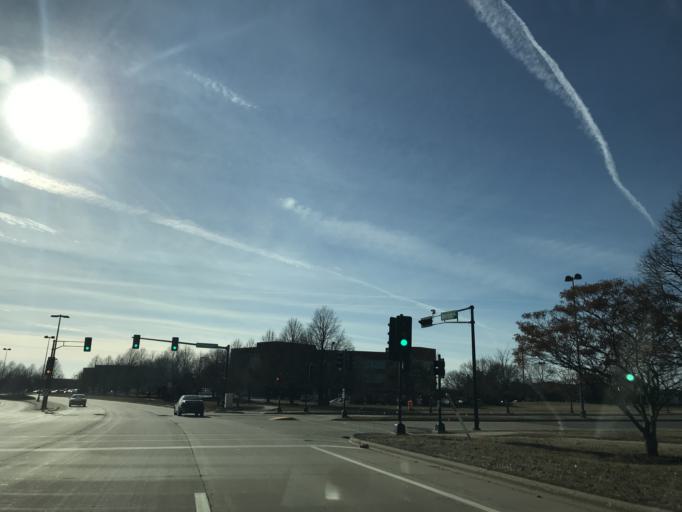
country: US
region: Wisconsin
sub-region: Dane County
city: Sun Prairie
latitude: 43.1507
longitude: -89.2894
